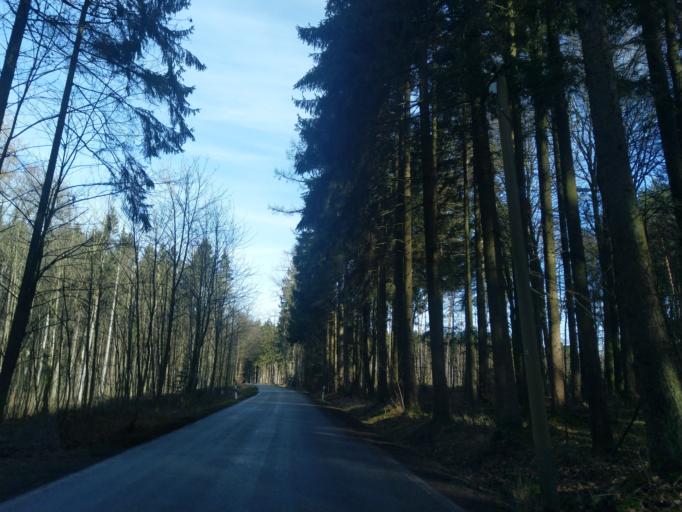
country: DE
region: Bavaria
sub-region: Lower Bavaria
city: Buchhofen
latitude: 48.6624
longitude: 12.9174
